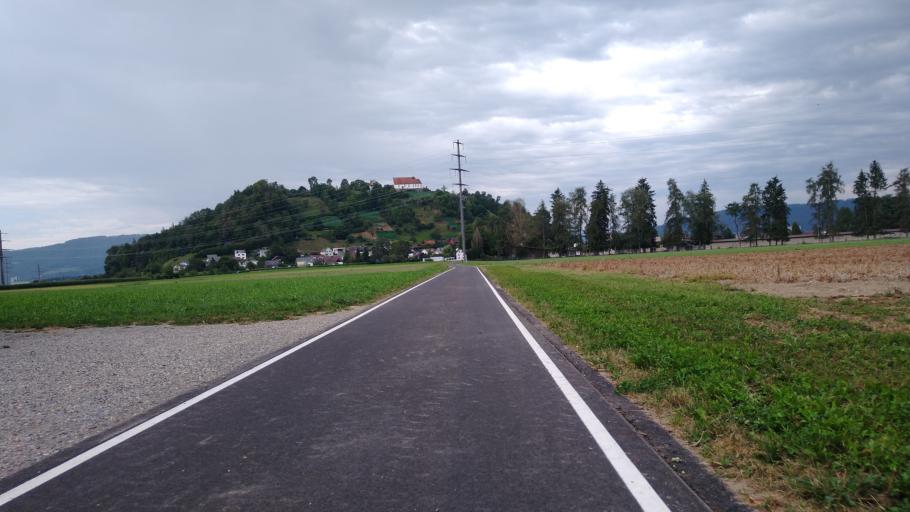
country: CH
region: Aargau
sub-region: Bezirk Lenzburg
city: Staufen
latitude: 47.3727
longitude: 8.1653
